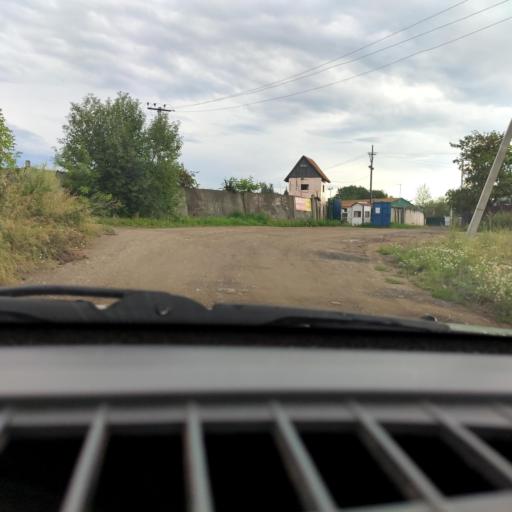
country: RU
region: Perm
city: Kondratovo
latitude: 58.0093
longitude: 56.0720
